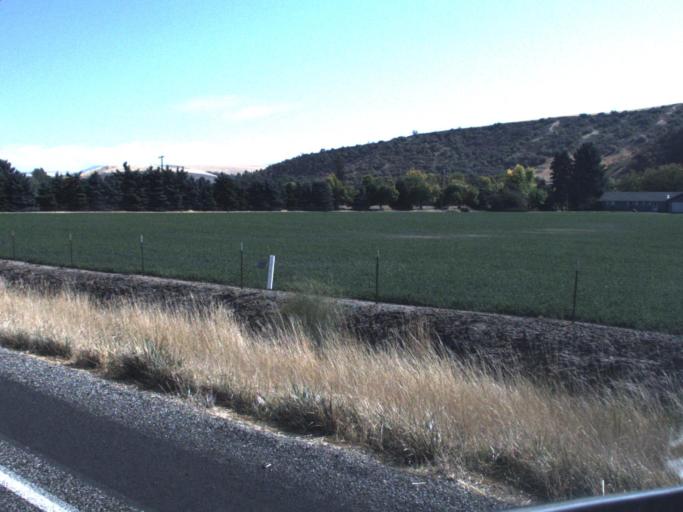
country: US
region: Washington
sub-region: Walla Walla County
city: Waitsburg
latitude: 46.2687
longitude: -118.1735
